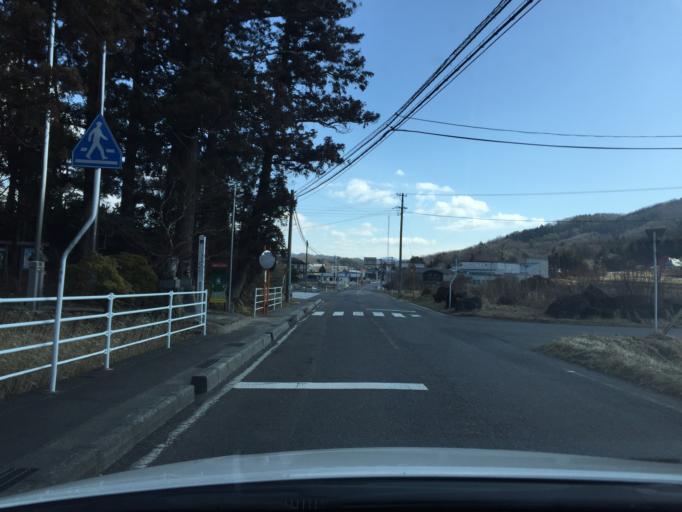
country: JP
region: Fukushima
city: Funehikimachi-funehiki
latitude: 37.3956
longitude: 140.5724
